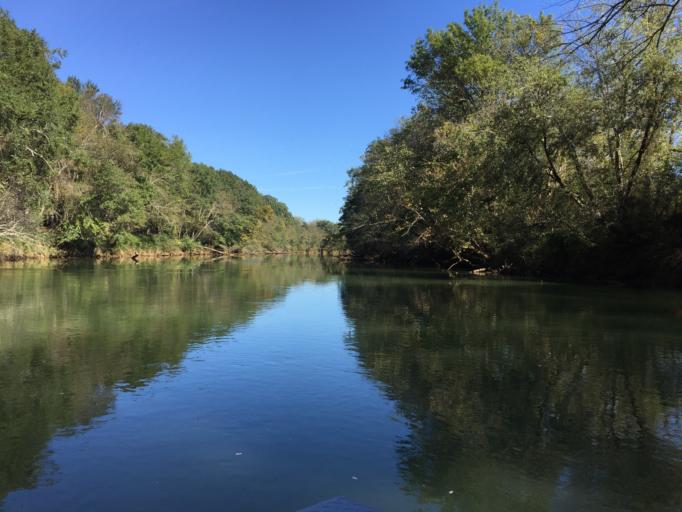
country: US
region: Georgia
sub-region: Fulton County
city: Johns Creek
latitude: 34.0200
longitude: -84.1754
